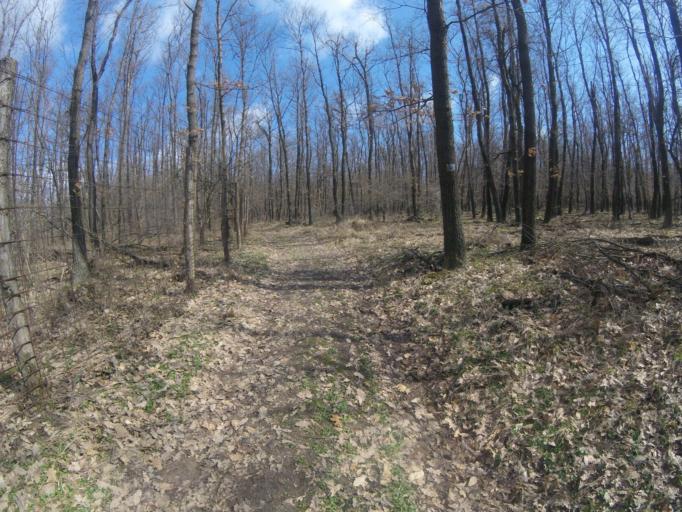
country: HU
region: Komarom-Esztergom
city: Tardos
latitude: 47.6721
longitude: 18.4769
